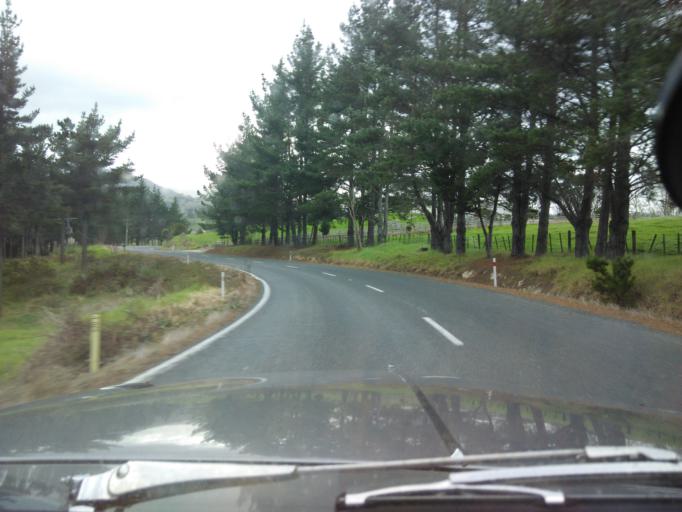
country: NZ
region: Auckland
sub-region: Auckland
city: Wellsford
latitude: -36.1731
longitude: 174.4171
